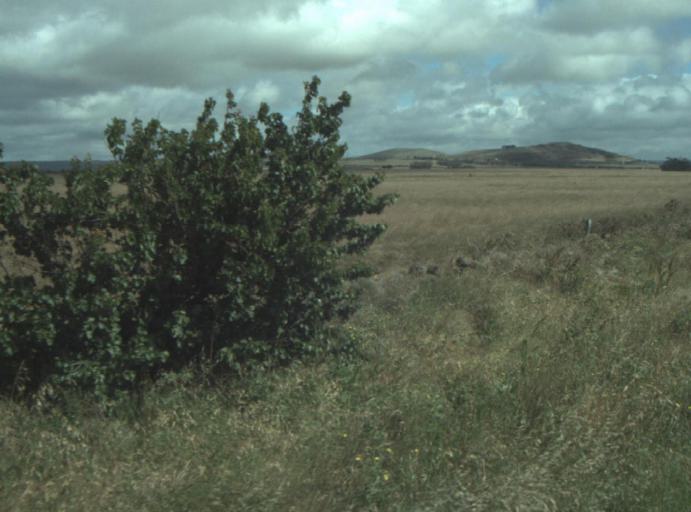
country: AU
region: Victoria
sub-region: Greater Geelong
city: Lara
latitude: -37.9422
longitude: 144.3095
